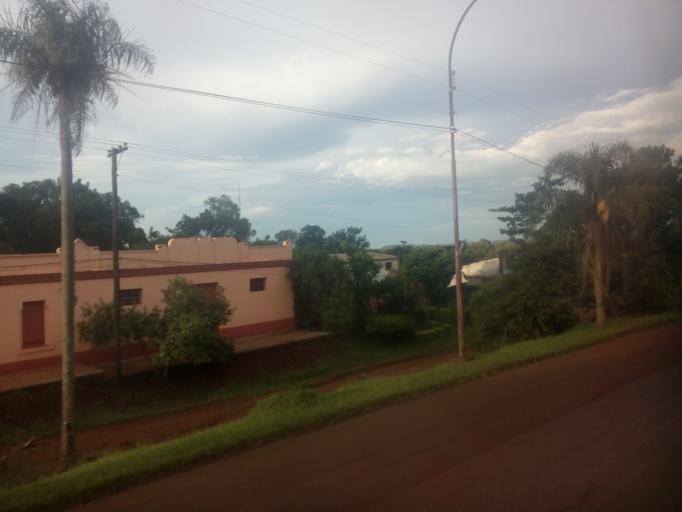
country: AR
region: Misiones
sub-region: Departamento de Obera
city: Obera
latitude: -27.4898
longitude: -55.1485
